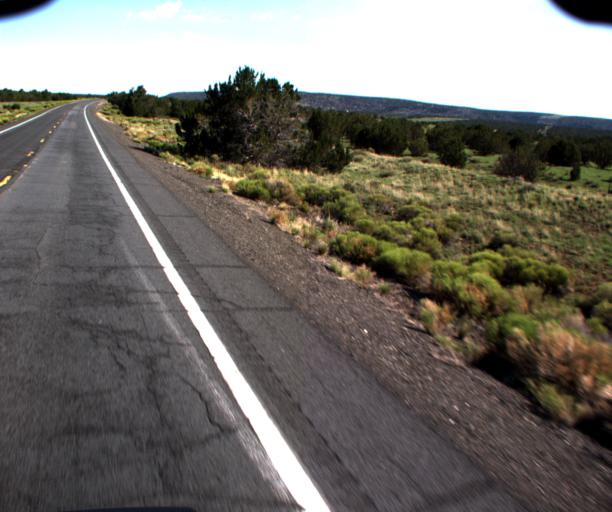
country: US
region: Arizona
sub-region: Coconino County
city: Williams
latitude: 35.4411
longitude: -112.1716
